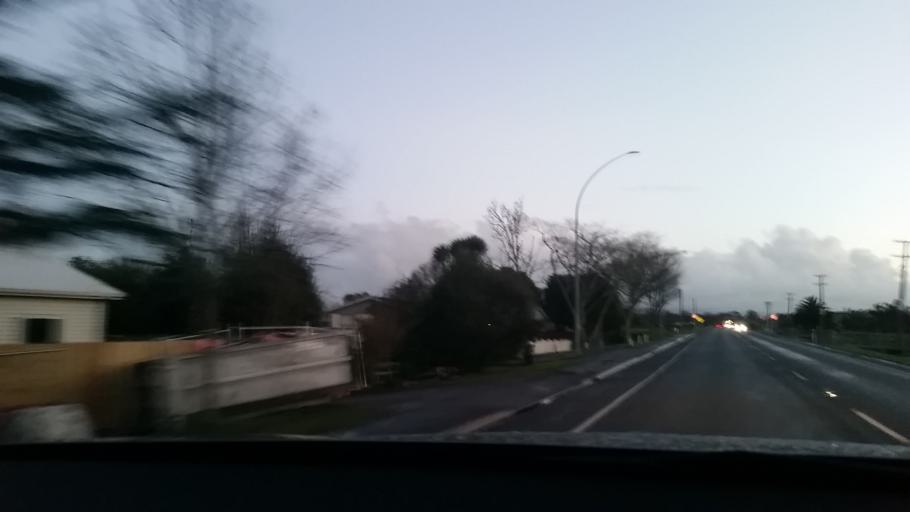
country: NZ
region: Waikato
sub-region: Hamilton City
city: Hamilton
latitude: -37.8058
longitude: 175.2413
